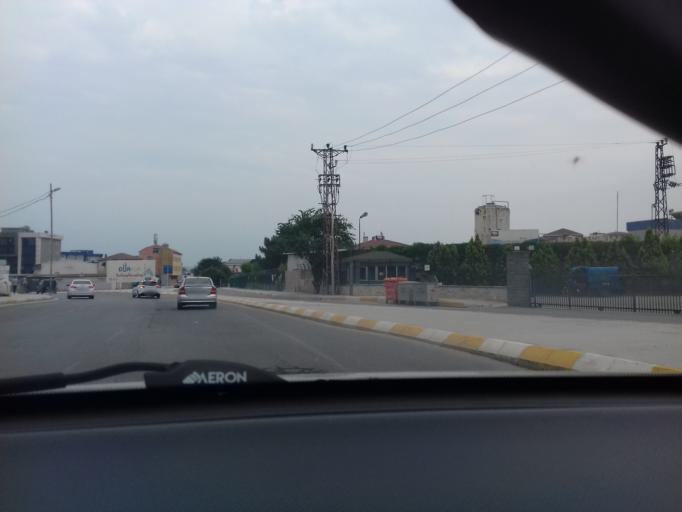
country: TR
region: Istanbul
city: Pendik
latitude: 40.9088
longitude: 29.2981
